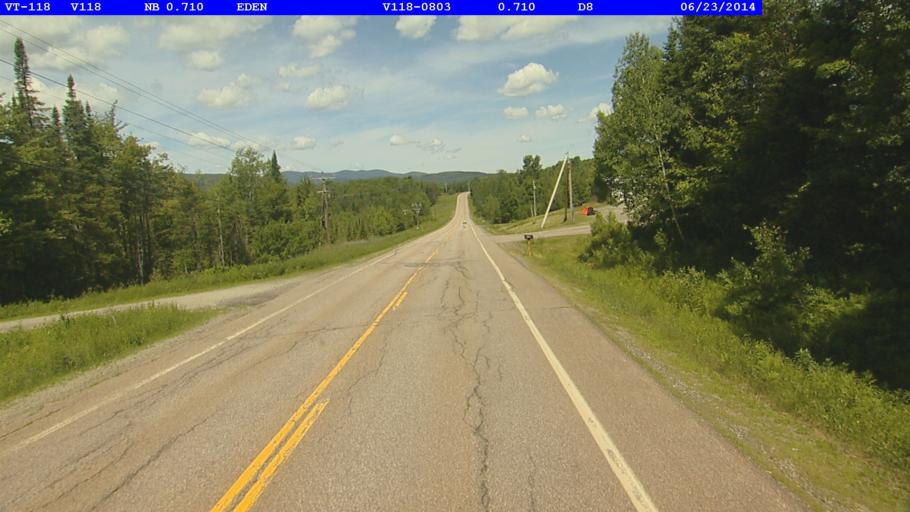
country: US
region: Vermont
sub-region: Lamoille County
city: Hyde Park
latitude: 44.7156
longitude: -72.5542
